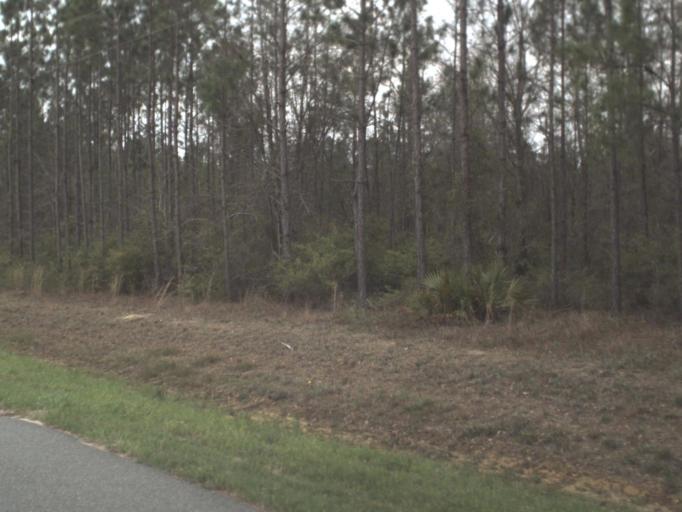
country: US
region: Florida
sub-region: Calhoun County
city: Blountstown
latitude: 30.3655
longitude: -85.2136
